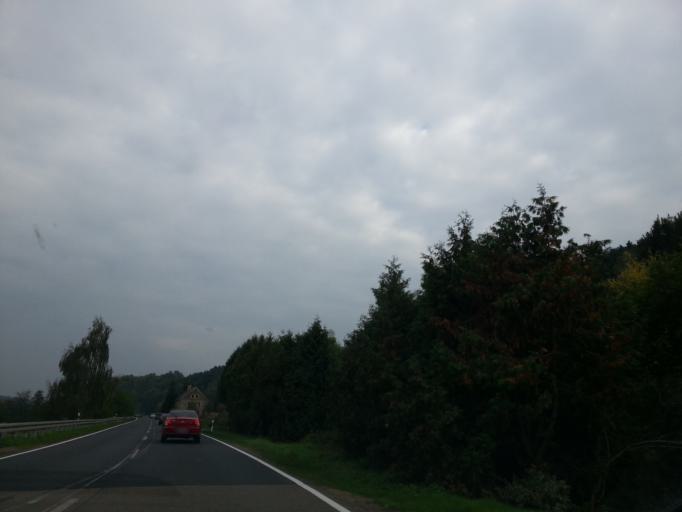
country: DE
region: Saxony
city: Meissen
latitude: 51.1909
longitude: 13.4209
